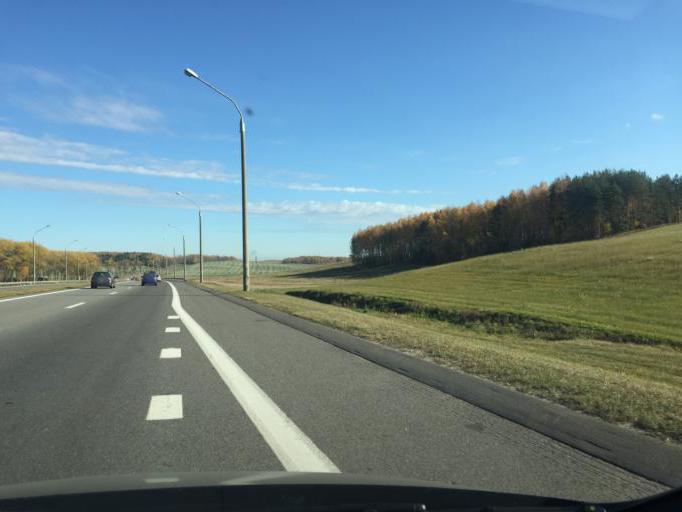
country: BY
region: Minsk
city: Slabada
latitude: 54.0173
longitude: 27.9020
